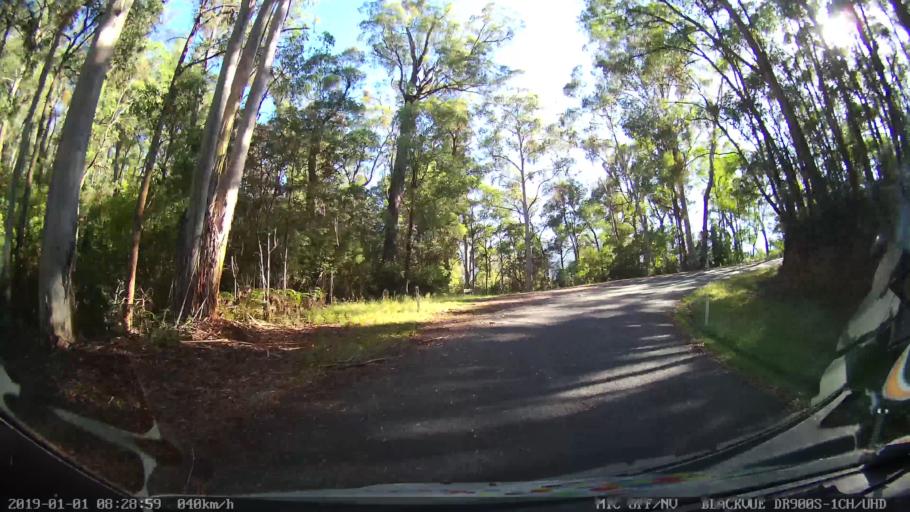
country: AU
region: New South Wales
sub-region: Snowy River
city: Jindabyne
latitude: -36.3735
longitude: 148.1914
